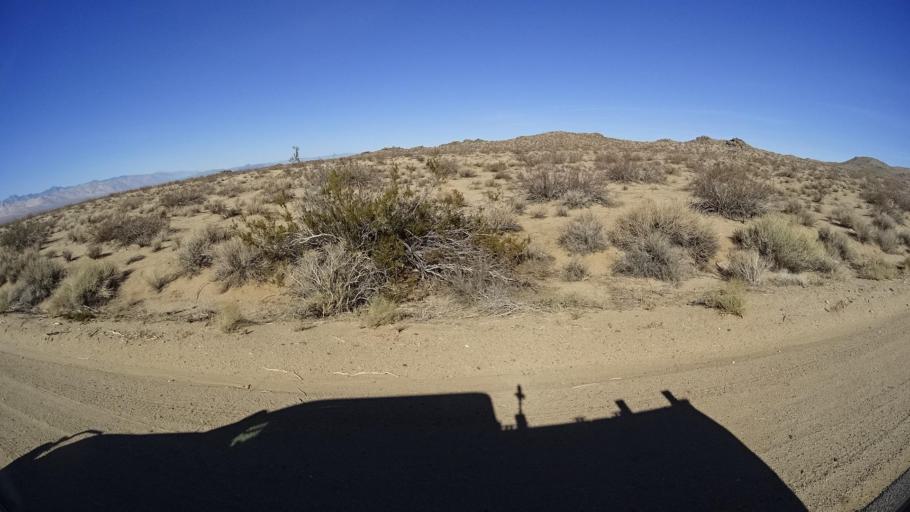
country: US
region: California
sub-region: Kern County
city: Ridgecrest
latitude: 35.5526
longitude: -117.7288
